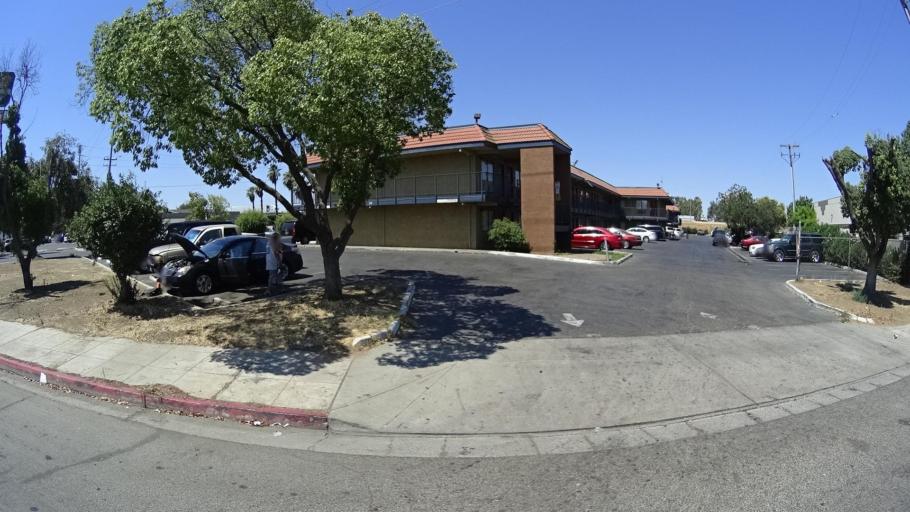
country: US
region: California
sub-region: Fresno County
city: Fresno
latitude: 36.7081
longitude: -119.7727
